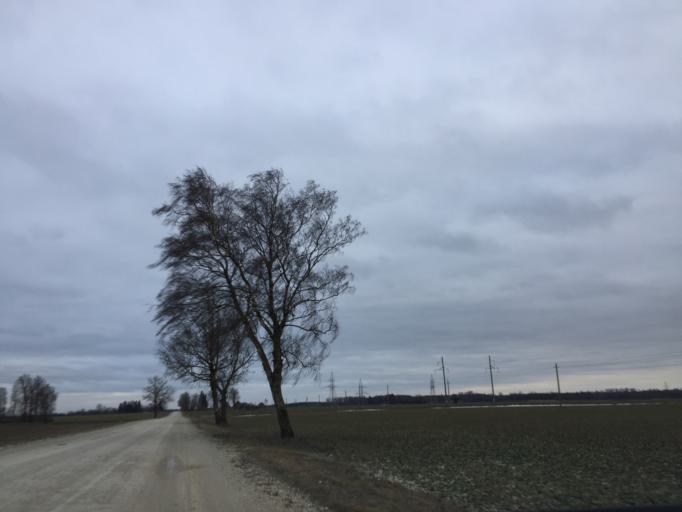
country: LT
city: Zagare
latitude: 56.3416
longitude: 23.2495
